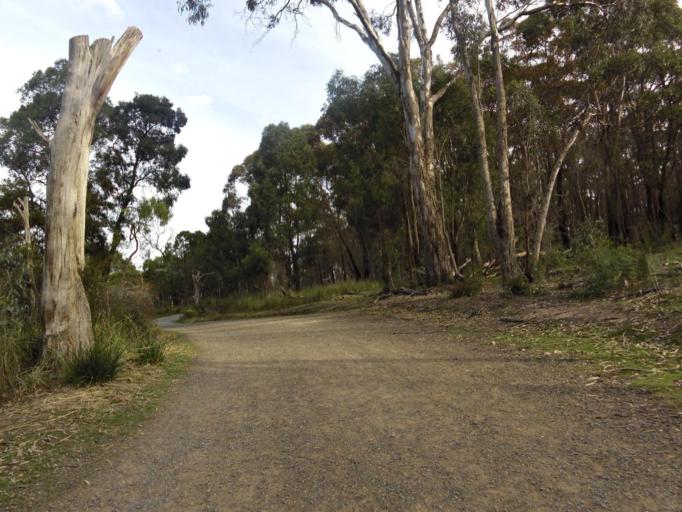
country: AU
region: Victoria
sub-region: Yarra Ranges
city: Lysterfield
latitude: -37.9562
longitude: 145.2948
